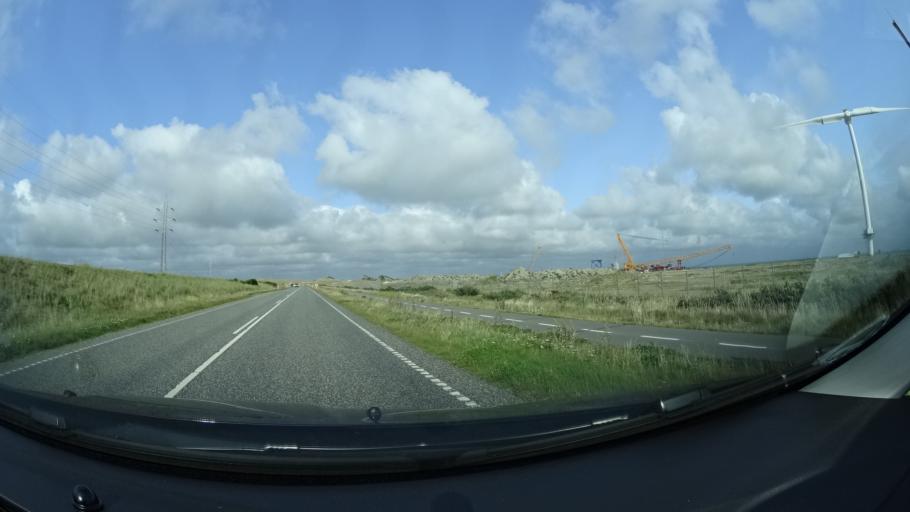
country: DK
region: Central Jutland
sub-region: Lemvig Kommune
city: Thyboron
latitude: 56.6761
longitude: 8.2190
